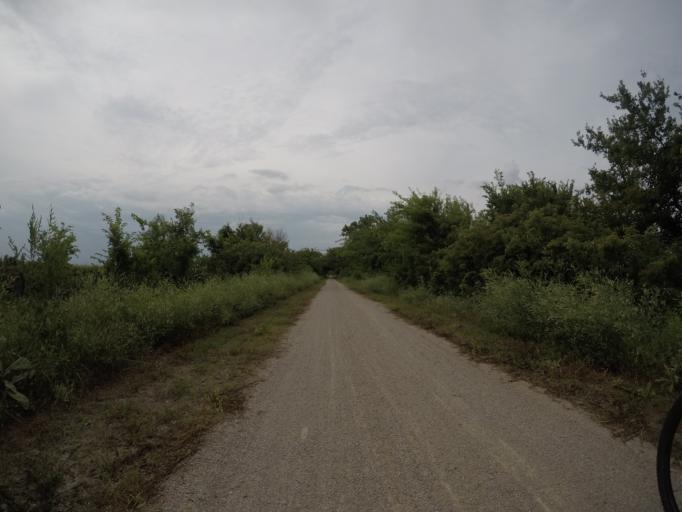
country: US
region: Kansas
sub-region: Franklin County
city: Ottawa
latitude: 38.5208
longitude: -95.2723
